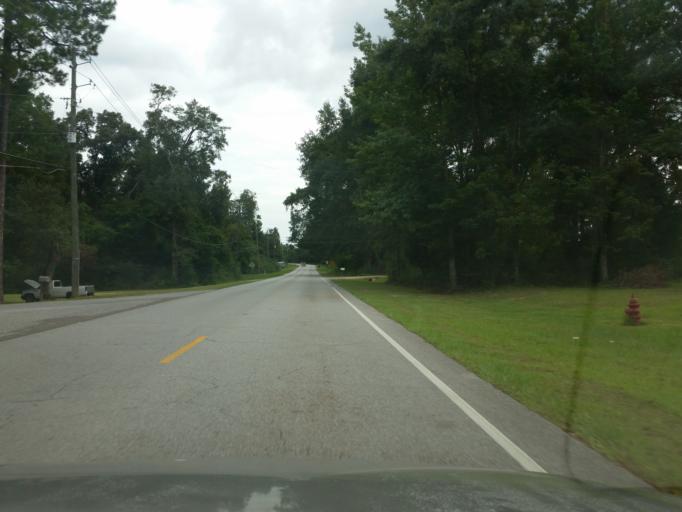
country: US
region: Florida
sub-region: Escambia County
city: Molino
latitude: 30.7011
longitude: -87.3336
